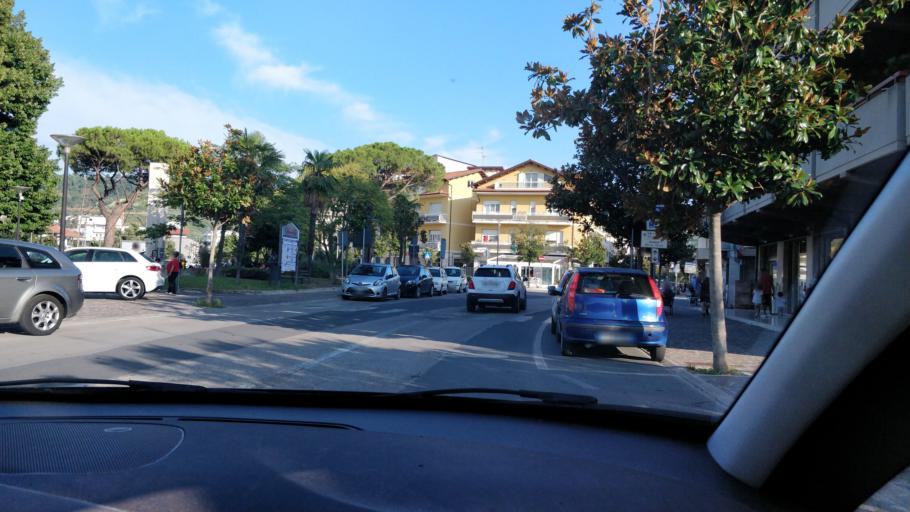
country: IT
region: Abruzzo
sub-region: Provincia di Chieti
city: Sambuceto
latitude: 42.4236
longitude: 14.1866
